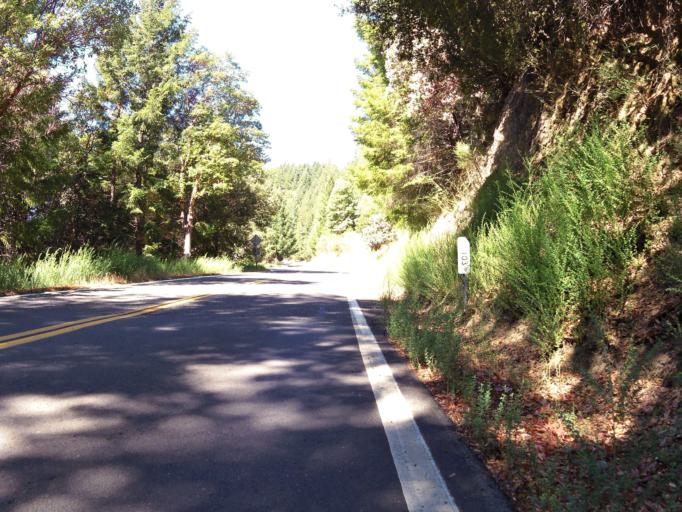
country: US
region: California
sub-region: Humboldt County
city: Redway
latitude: 39.8490
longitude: -123.7352
